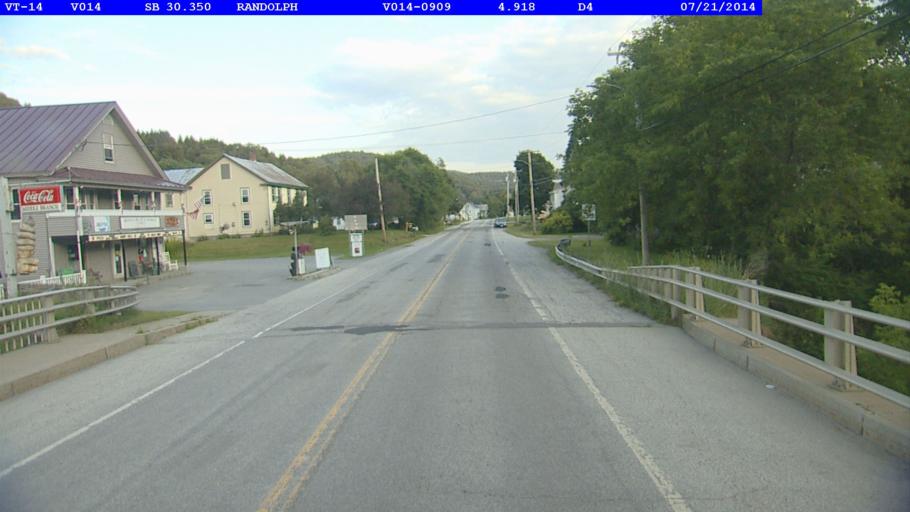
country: US
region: Vermont
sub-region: Orange County
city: Randolph
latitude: 43.9401
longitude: -72.5542
